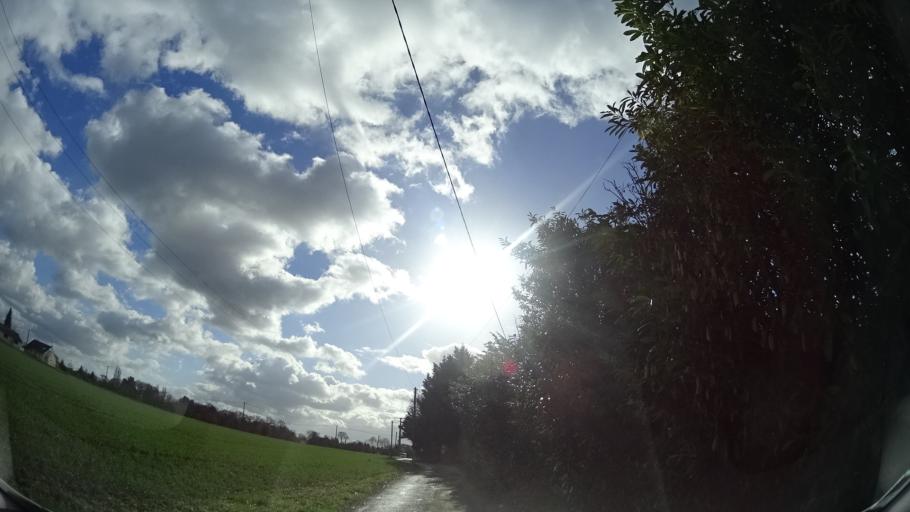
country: FR
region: Brittany
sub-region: Departement d'Ille-et-Vilaine
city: Chantepie
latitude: 48.0766
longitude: -1.6420
